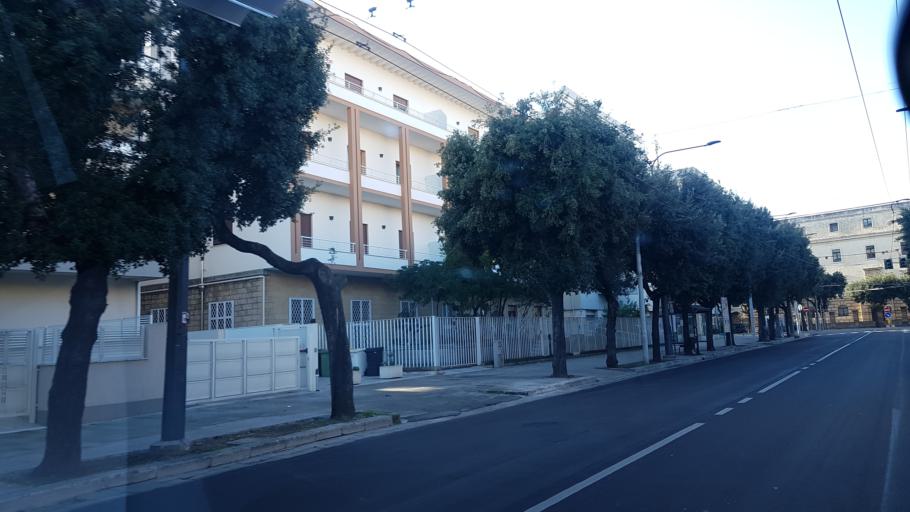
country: IT
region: Apulia
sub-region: Provincia di Lecce
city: Lecce
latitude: 40.3501
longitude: 18.1645
